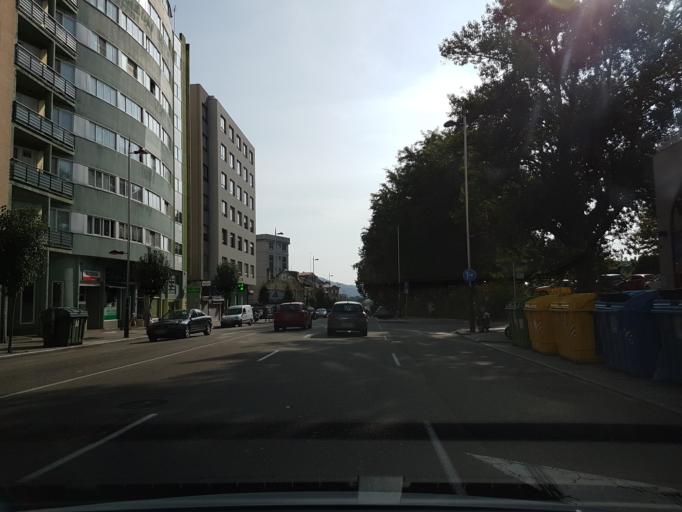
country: ES
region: Galicia
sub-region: Provincia de Pontevedra
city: Vigo
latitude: 42.2144
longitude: -8.7423
